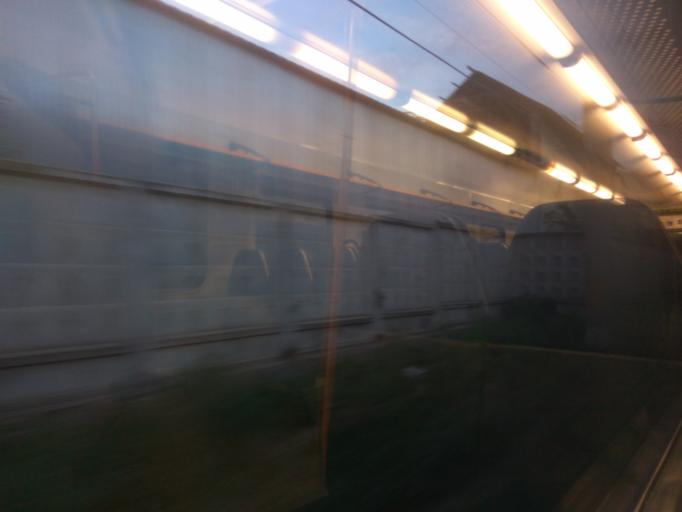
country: RU
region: Moscow
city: Solntsevo
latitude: 55.6440
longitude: 37.3798
